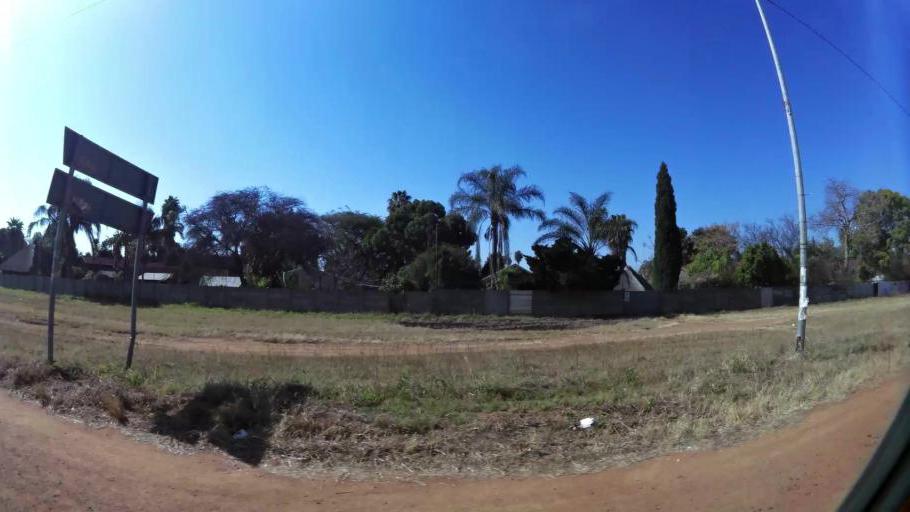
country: ZA
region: North-West
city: Ga-Rankuwa
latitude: -25.6500
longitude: 28.1024
